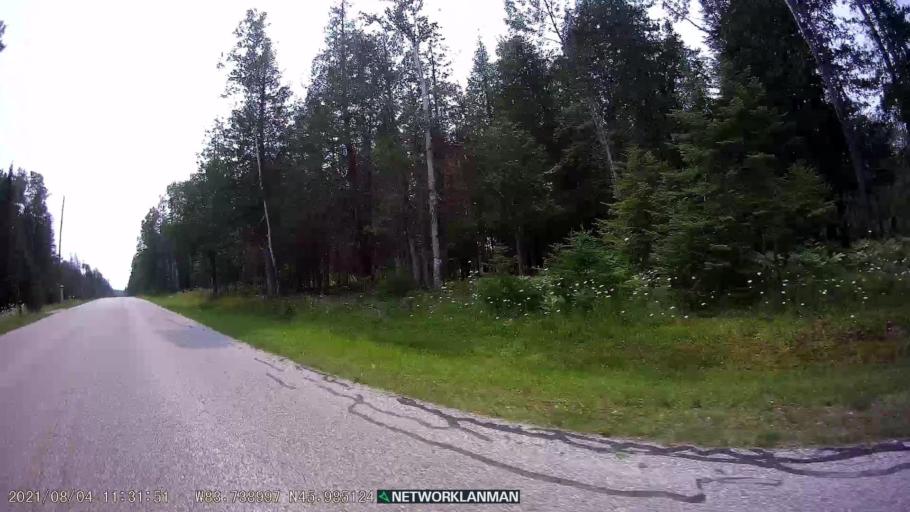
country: CA
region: Ontario
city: Thessalon
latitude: 45.9844
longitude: -83.7390
